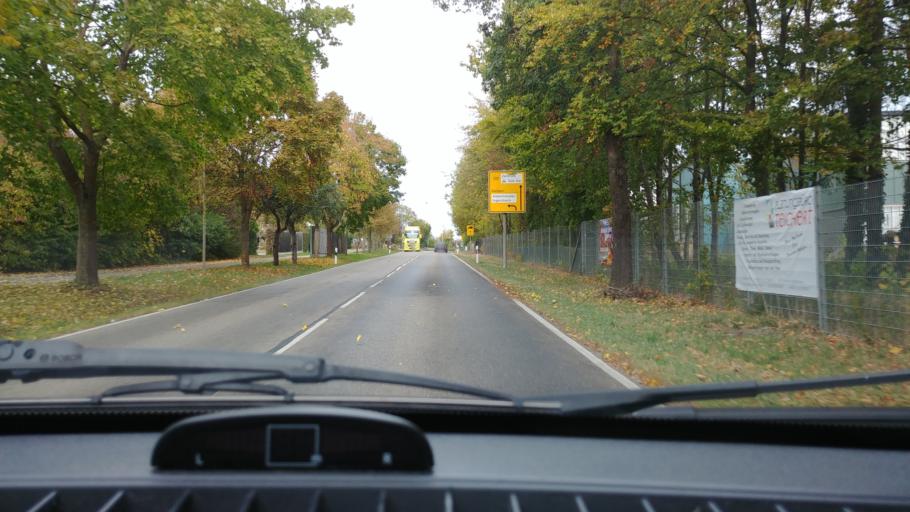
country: DE
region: Baden-Wuerttemberg
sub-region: Regierungsbezirk Stuttgart
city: Crailsheim
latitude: 49.1194
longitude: 10.0832
